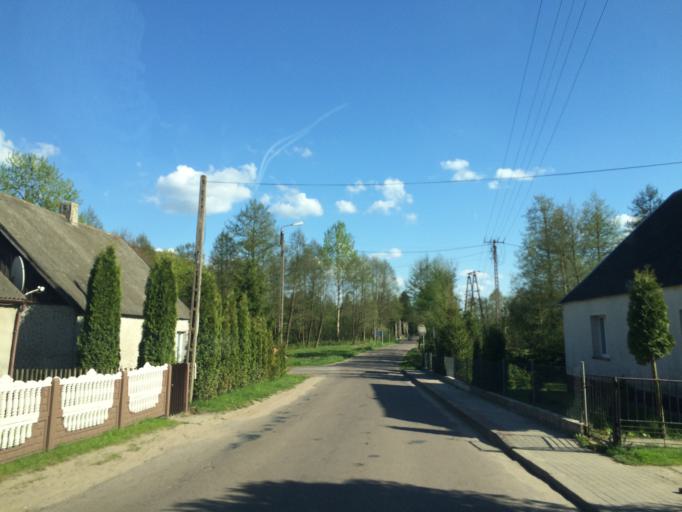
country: PL
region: Warmian-Masurian Voivodeship
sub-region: Powiat dzialdowski
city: Rybno
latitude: 53.4161
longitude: 19.9349
